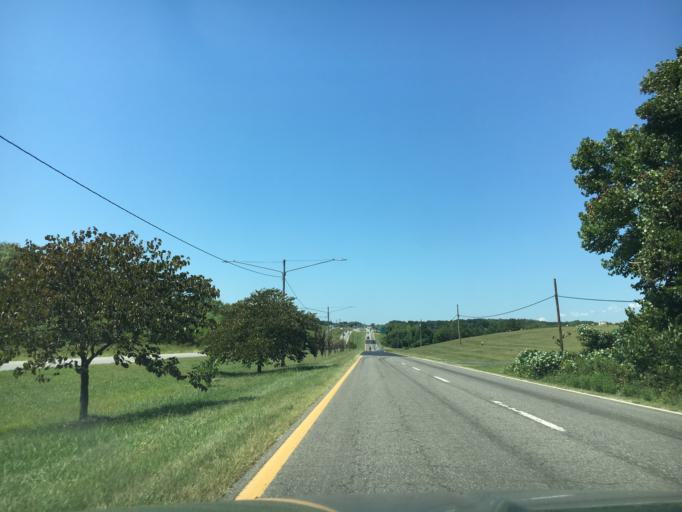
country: US
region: Virginia
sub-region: City of Danville
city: Danville
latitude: 36.5810
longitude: -79.3252
